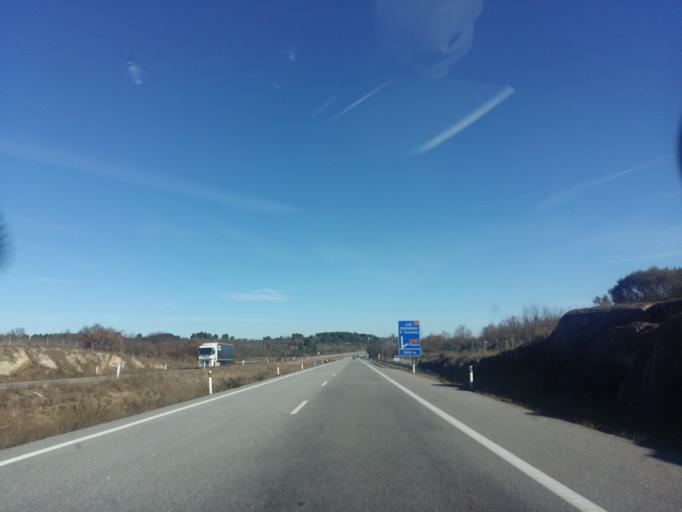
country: PT
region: Guarda
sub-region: Guarda
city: Sequeira
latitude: 40.6033
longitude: -7.0835
